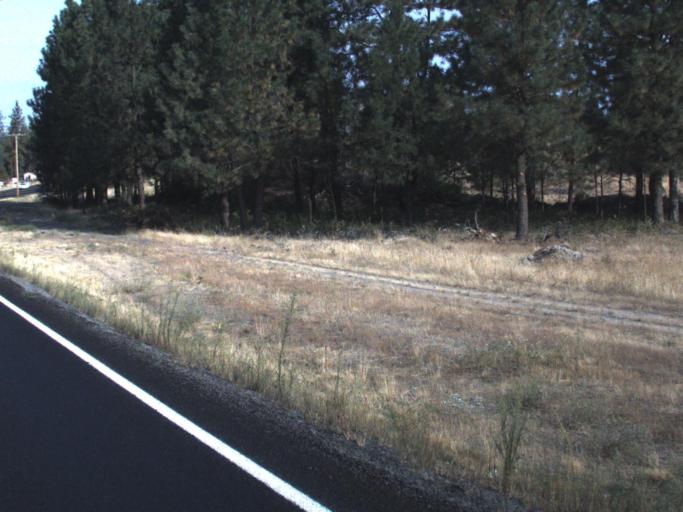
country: US
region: Washington
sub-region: Spokane County
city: Deer Park
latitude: 47.8323
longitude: -117.6019
